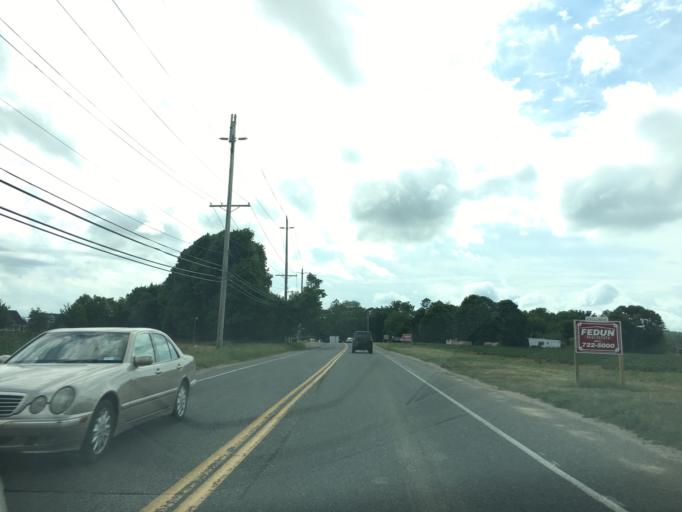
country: US
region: New York
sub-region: Suffolk County
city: Northville
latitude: 40.9680
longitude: -72.6429
